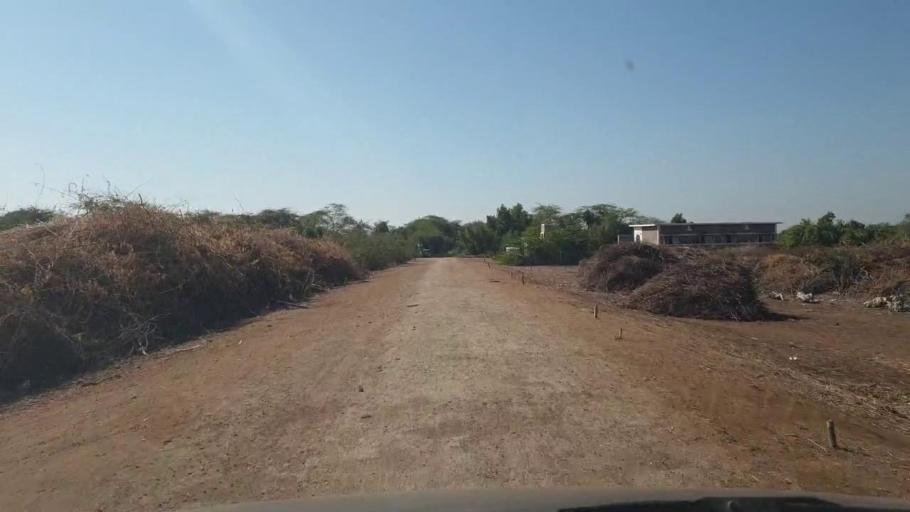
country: PK
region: Sindh
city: Umarkot
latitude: 25.3791
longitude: 69.6806
